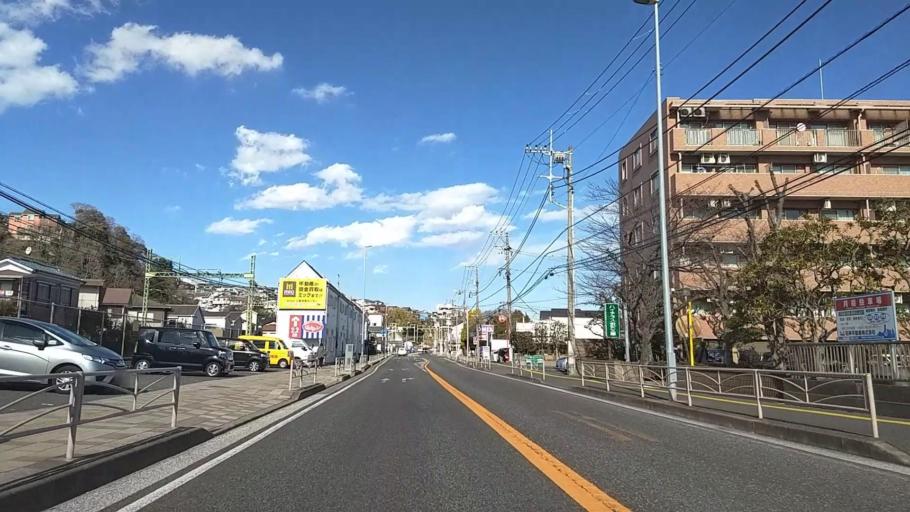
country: JP
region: Kanagawa
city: Zushi
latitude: 35.3477
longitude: 139.6241
